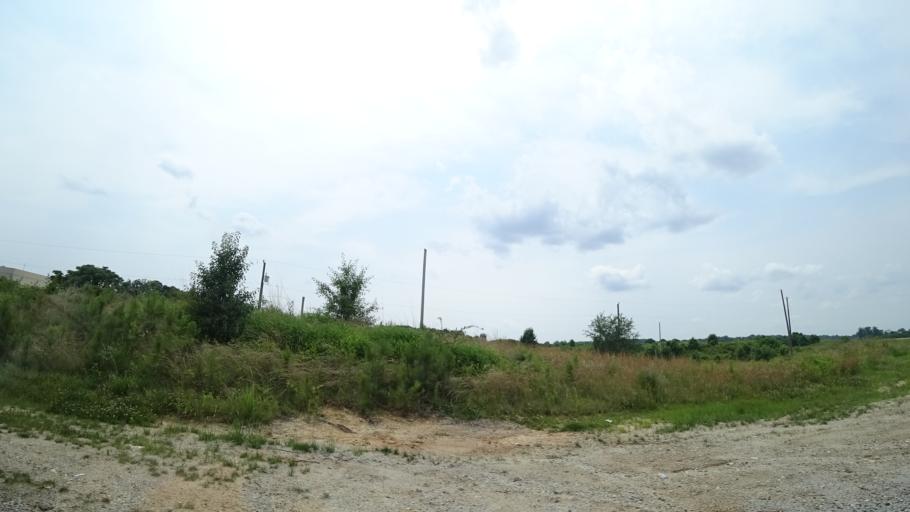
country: US
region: Virginia
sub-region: Fairfax County
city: Lorton
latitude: 38.6998
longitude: -77.2397
